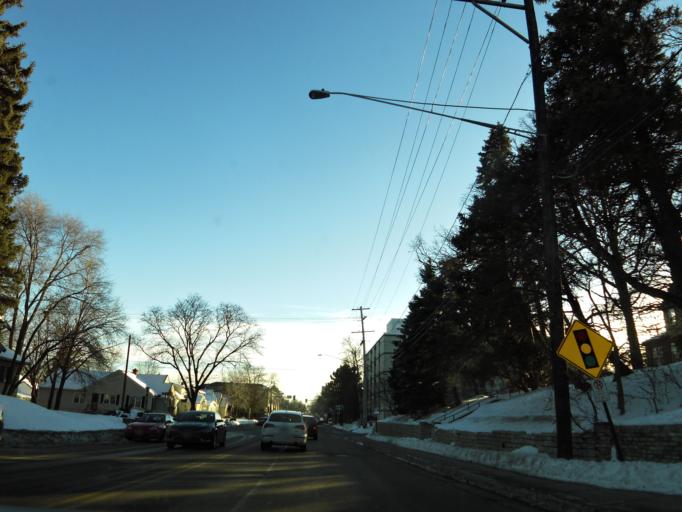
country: US
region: Minnesota
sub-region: Hennepin County
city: Edina
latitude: 44.9148
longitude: -93.3291
